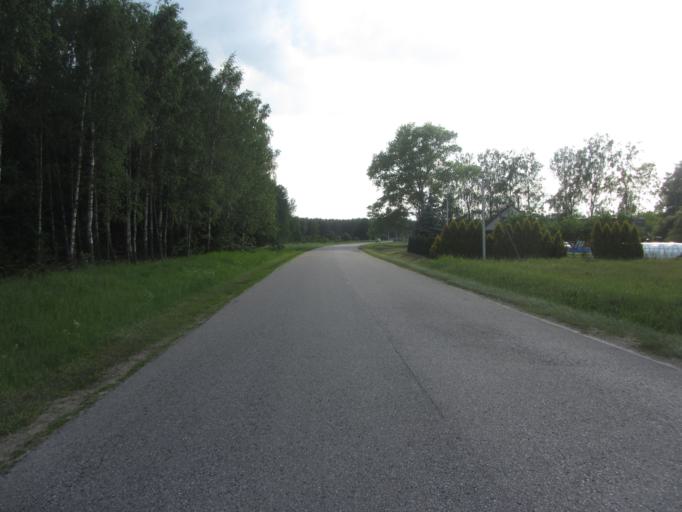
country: LT
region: Kauno apskritis
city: Jonava
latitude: 55.1062
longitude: 24.4039
